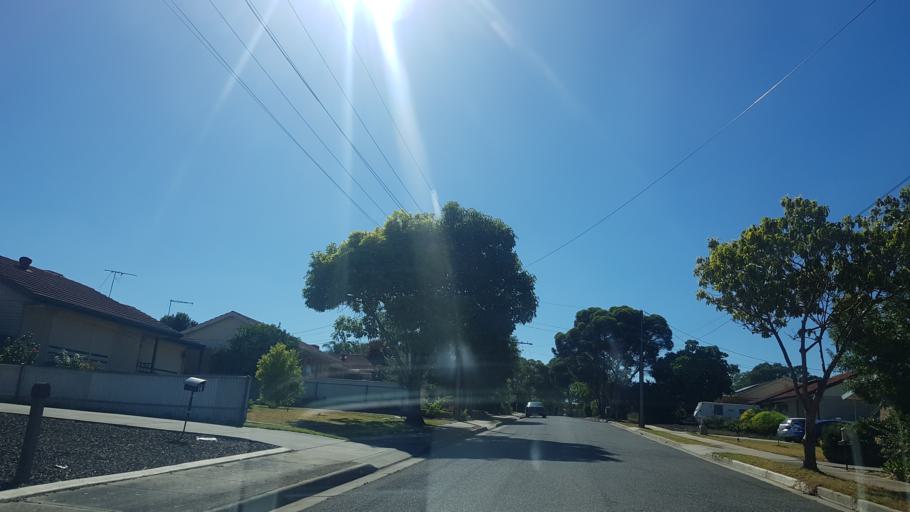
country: AU
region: South Australia
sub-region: Salisbury
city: Ingle Farm
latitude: -34.8252
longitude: 138.6496
